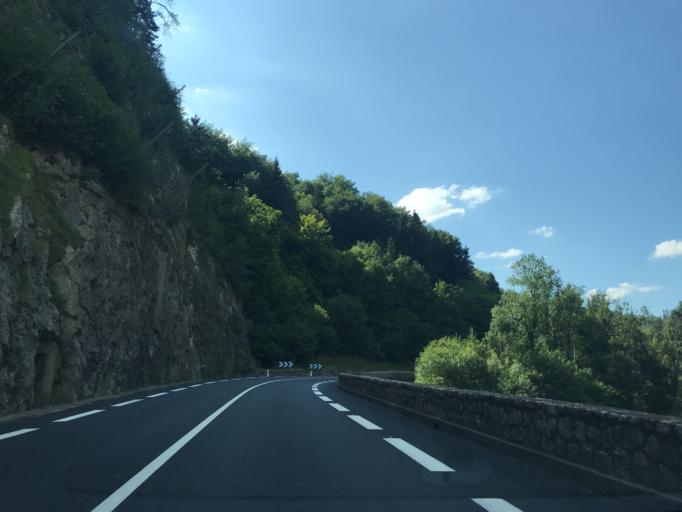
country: FR
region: Rhone-Alpes
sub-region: Departement de la Haute-Savoie
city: Dingy-Saint-Clair
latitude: 45.9052
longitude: 6.2063
